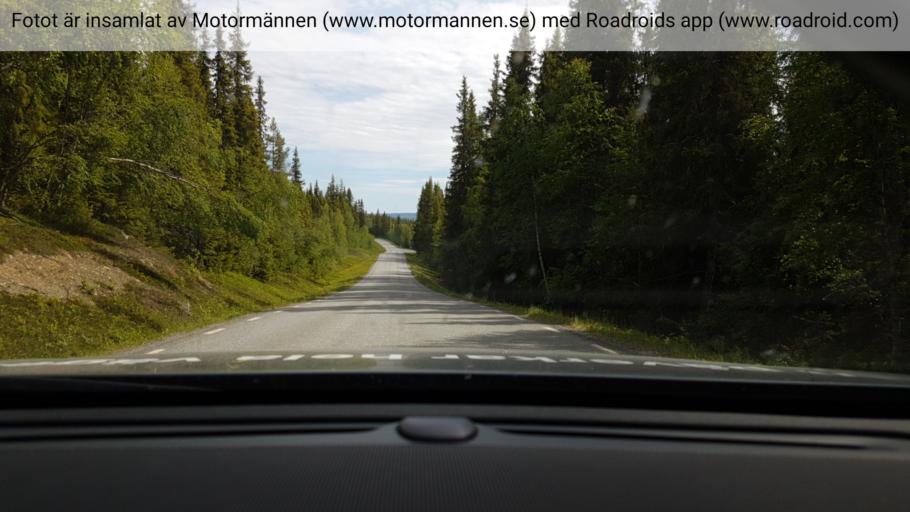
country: SE
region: Vaesterbotten
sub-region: Vilhelmina Kommun
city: Sjoberg
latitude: 65.2203
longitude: 16.0292
